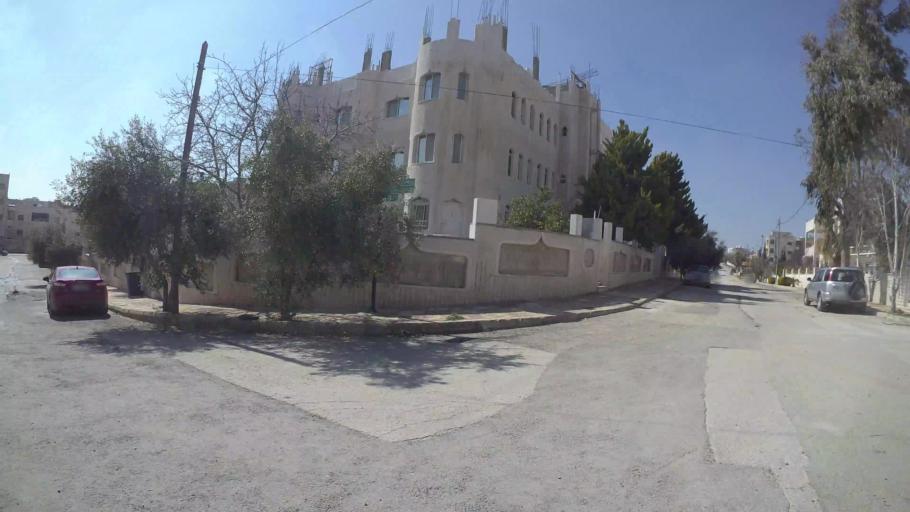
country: JO
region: Amman
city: Al Bunayyat ash Shamaliyah
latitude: 31.9002
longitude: 35.8983
